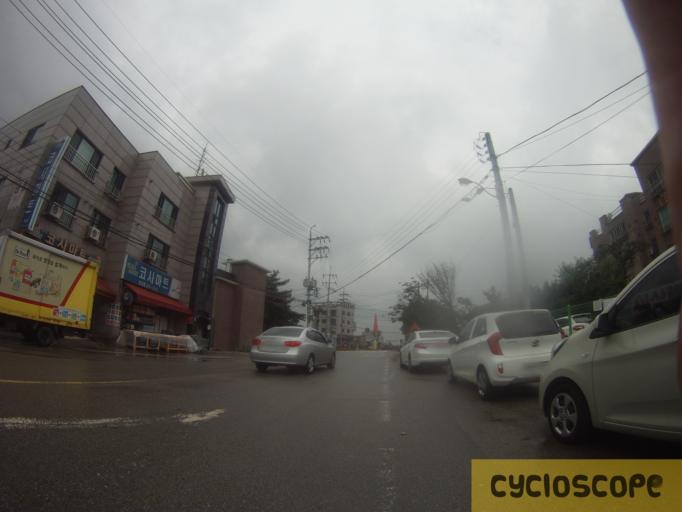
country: KR
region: Gyeonggi-do
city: Hwaseong-si
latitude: 37.0880
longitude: 126.8017
